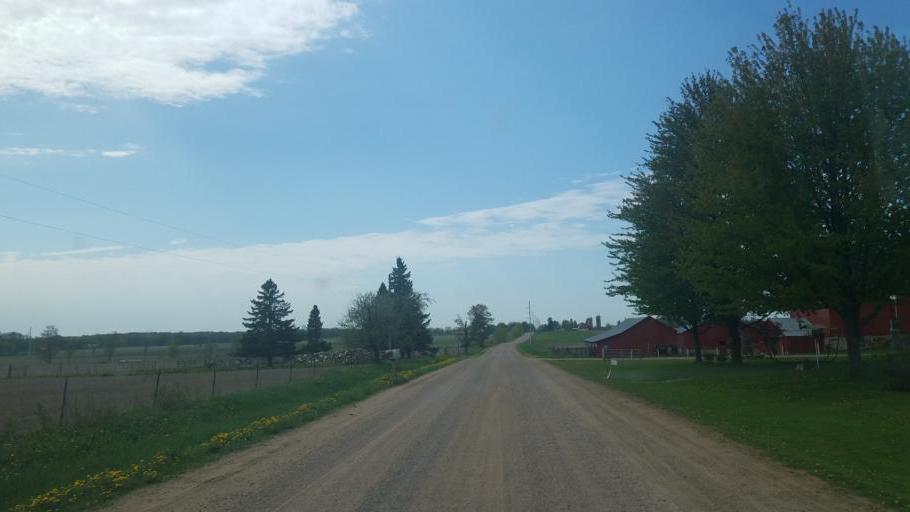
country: US
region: Wisconsin
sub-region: Marathon County
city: Spencer
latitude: 44.6362
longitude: -90.3767
